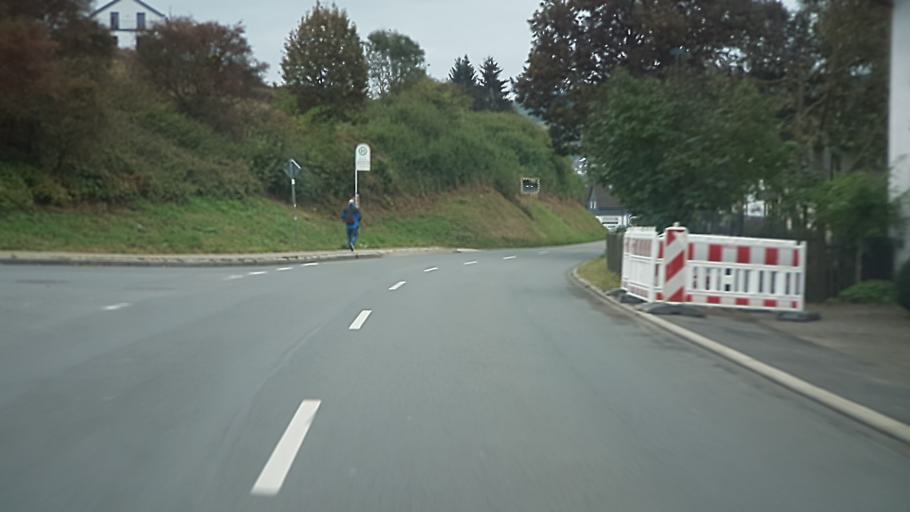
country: DE
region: North Rhine-Westphalia
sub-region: Regierungsbezirk Arnsberg
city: Attendorn
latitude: 51.1331
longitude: 7.8923
